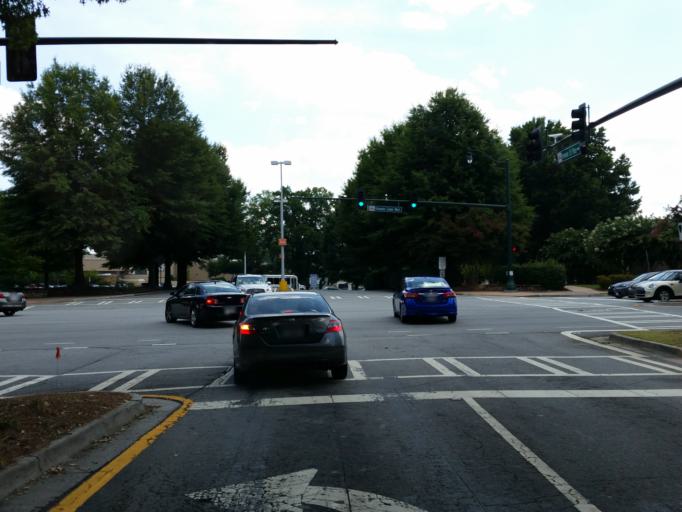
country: US
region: Georgia
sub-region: DeKalb County
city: Dunwoody
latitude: 33.9273
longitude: -84.3416
